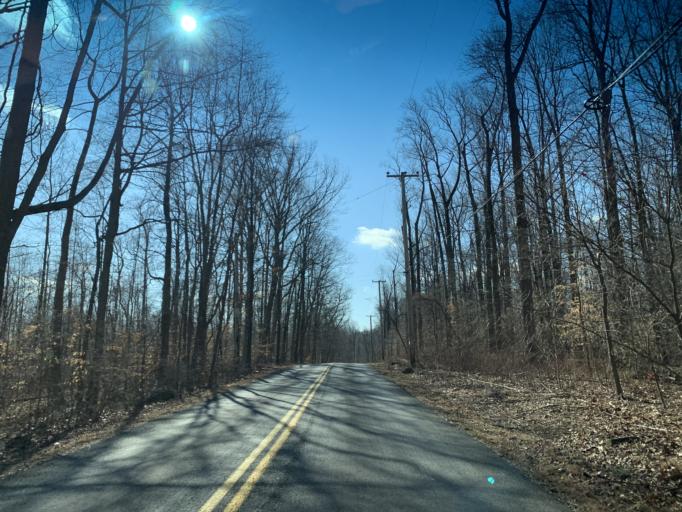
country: US
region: Maryland
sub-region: Harford County
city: Riverside
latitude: 39.5082
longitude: -76.2356
